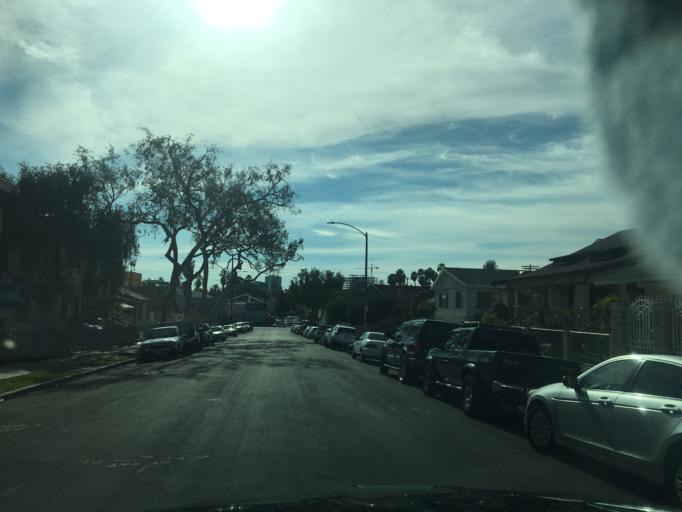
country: US
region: California
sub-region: Los Angeles County
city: Silver Lake
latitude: 34.0738
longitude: -118.2833
